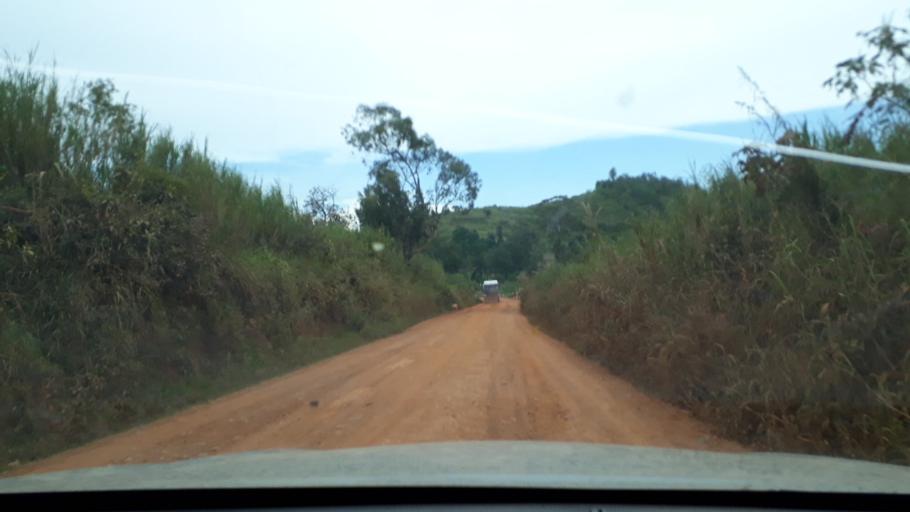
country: CD
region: Eastern Province
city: Bunia
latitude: 1.8289
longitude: 30.4481
